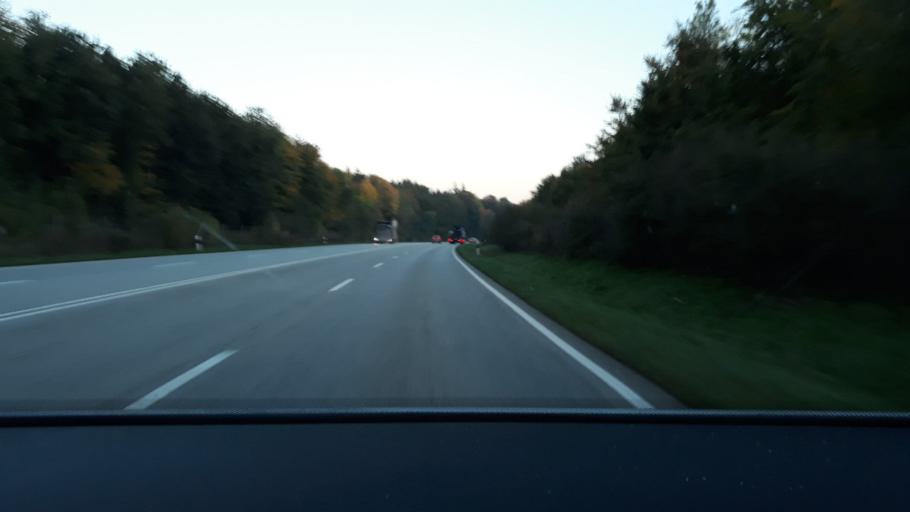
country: DE
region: Schleswig-Holstein
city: Schuby
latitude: 54.5157
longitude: 9.5137
